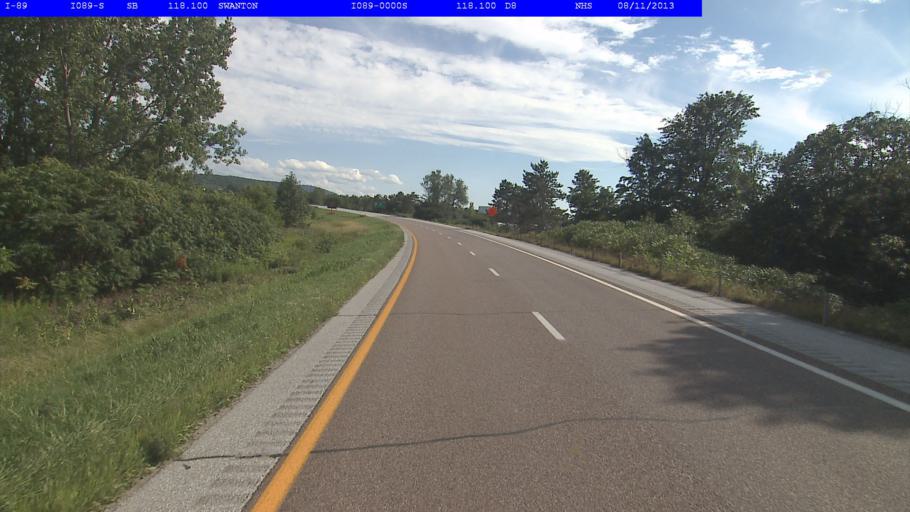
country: US
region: Vermont
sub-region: Franklin County
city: Saint Albans
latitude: 44.8496
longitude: -73.0836
